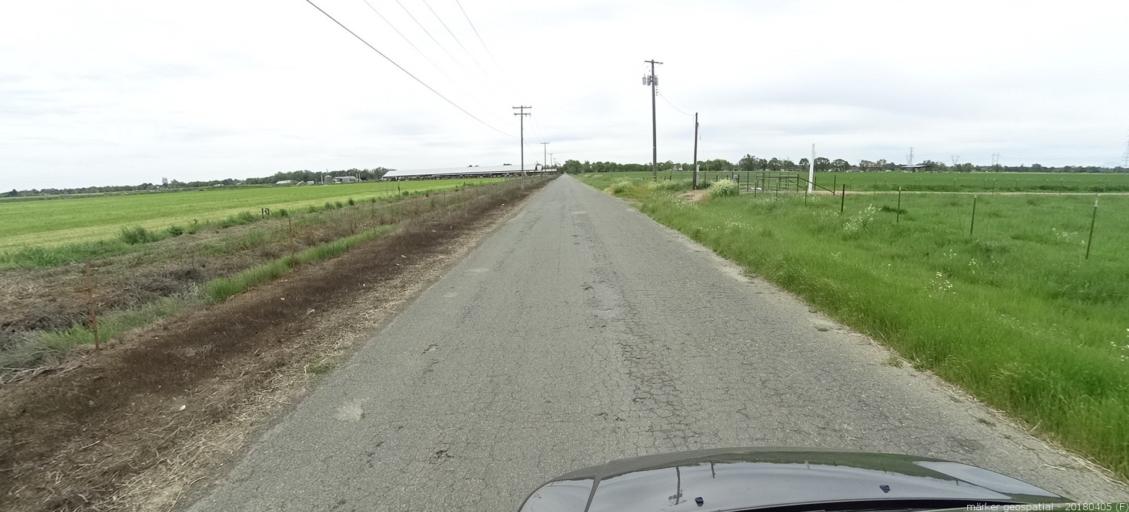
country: US
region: California
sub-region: Sacramento County
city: Galt
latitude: 38.2888
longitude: -121.3514
